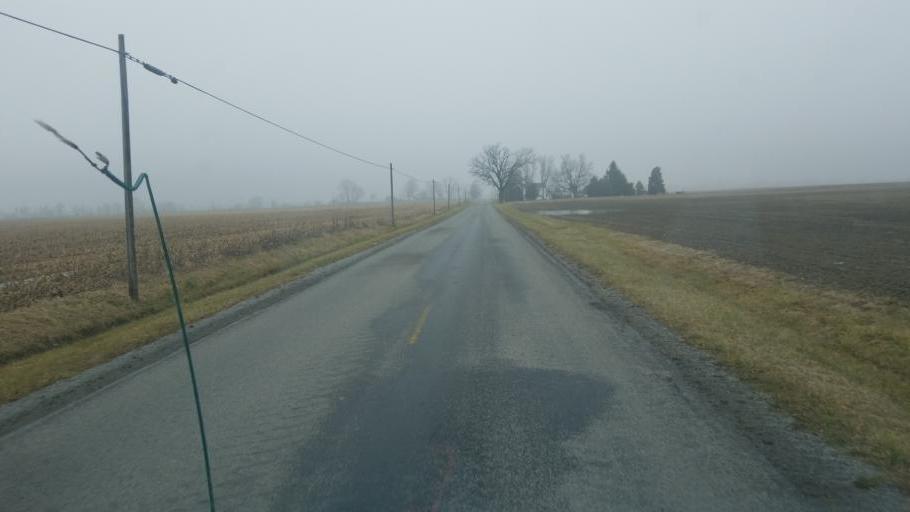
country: US
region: Ohio
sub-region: Hardin County
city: Kenton
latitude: 40.5138
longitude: -83.5225
